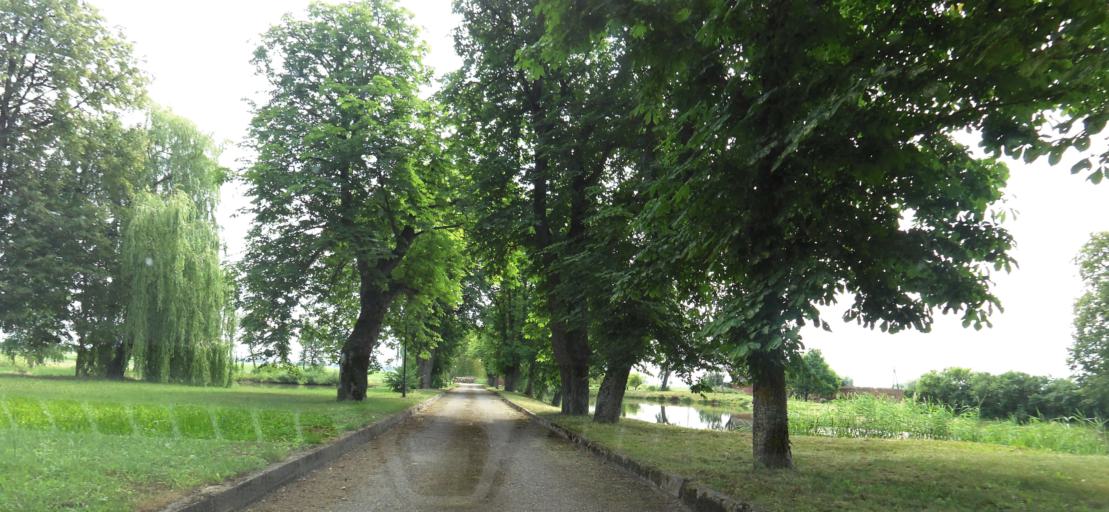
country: LT
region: Panevezys
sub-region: Birzai
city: Birzai
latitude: 56.2888
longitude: 24.6054
